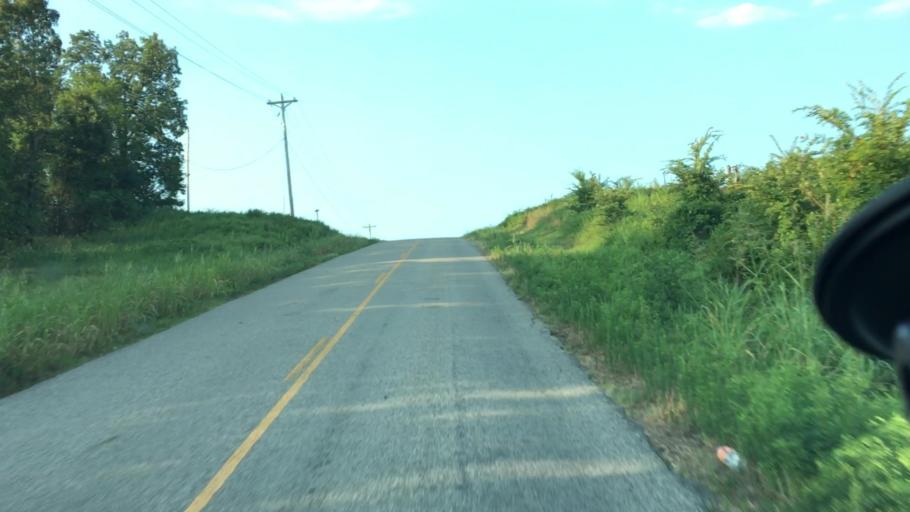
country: US
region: Arkansas
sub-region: Johnson County
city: Coal Hill
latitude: 35.3583
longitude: -93.6131
